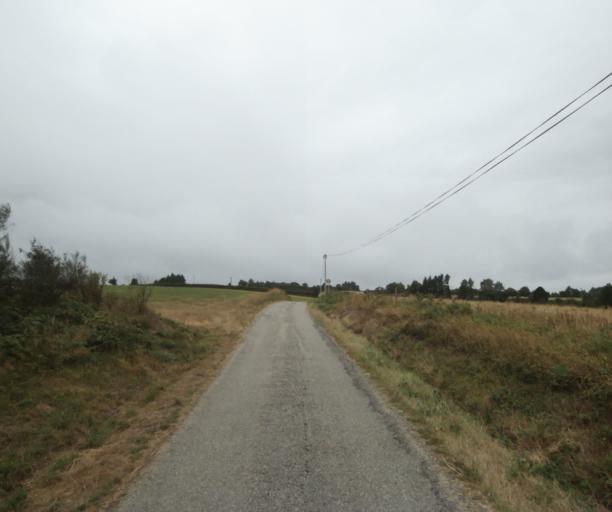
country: FR
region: Midi-Pyrenees
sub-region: Departement du Tarn
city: Soreze
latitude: 43.4128
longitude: 2.0520
